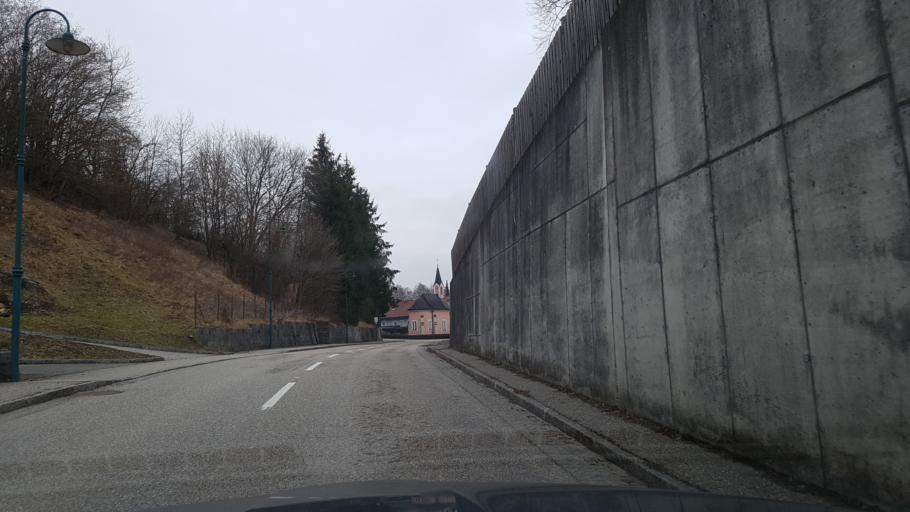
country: AT
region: Salzburg
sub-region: Politischer Bezirk Salzburg-Umgebung
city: Dorfbeuern
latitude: 48.0648
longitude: 12.9625
